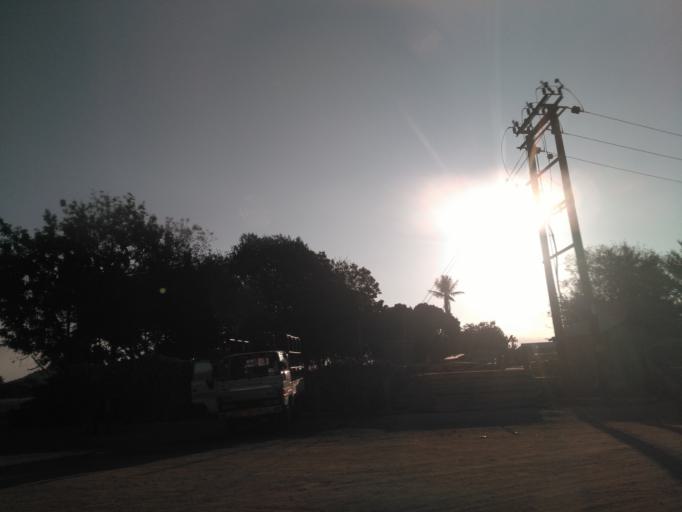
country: TZ
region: Dodoma
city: Dodoma
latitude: -6.1717
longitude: 35.7439
